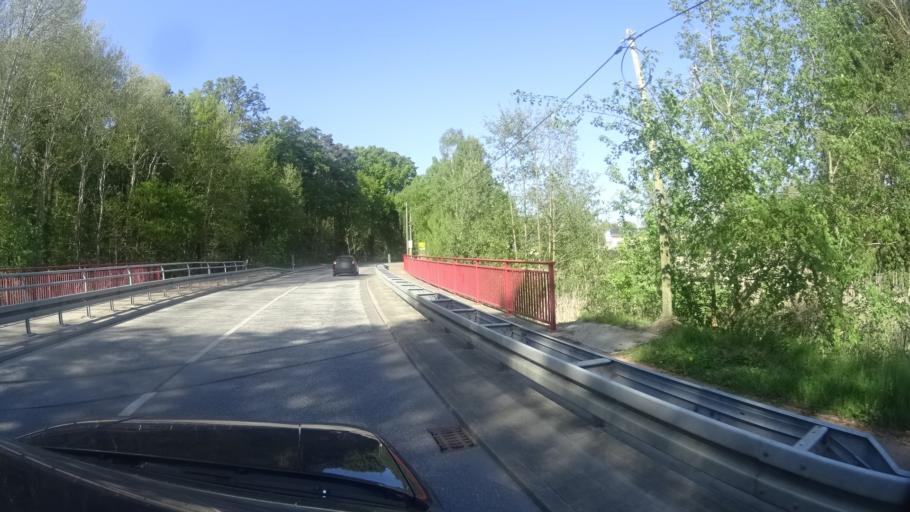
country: DE
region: Mecklenburg-Vorpommern
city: Seeheilbad Graal-Muritz
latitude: 54.2429
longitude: 12.2251
